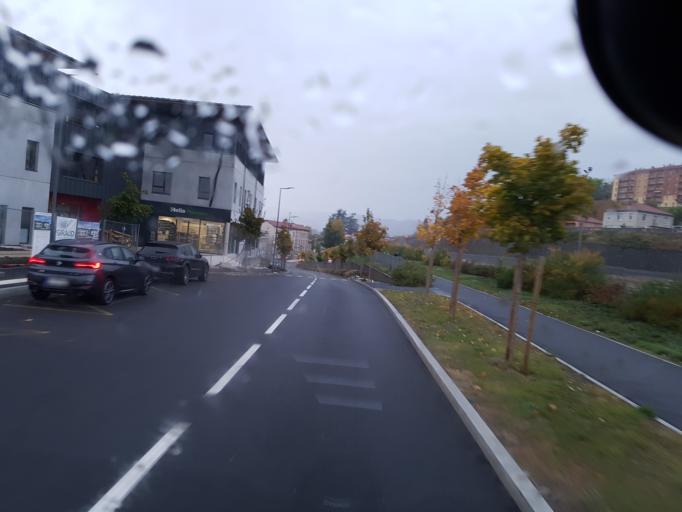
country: FR
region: Auvergne
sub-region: Departement de la Haute-Loire
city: Le Puy-en-Velay
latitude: 45.0456
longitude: 3.8964
